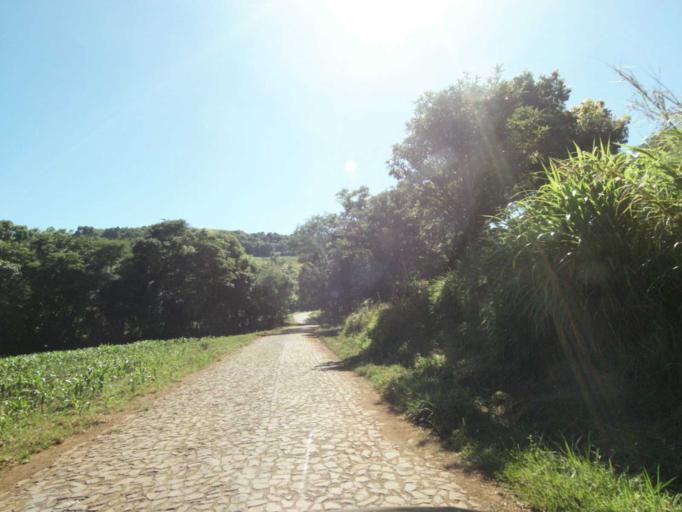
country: BR
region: Parana
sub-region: Francisco Beltrao
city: Francisco Beltrao
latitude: -26.1469
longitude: -53.3061
